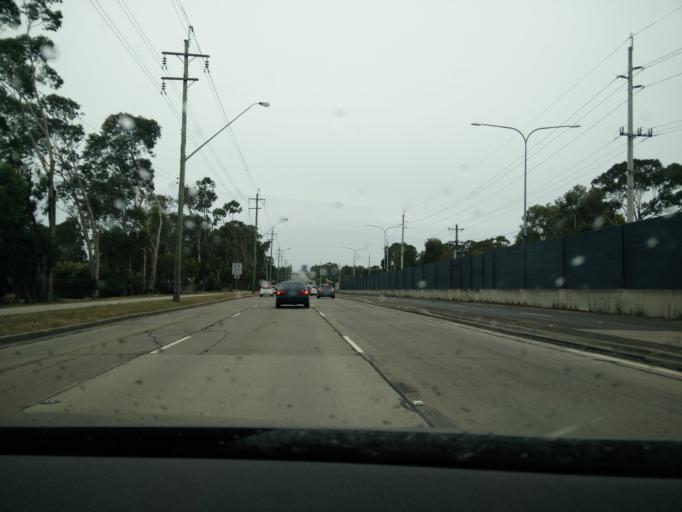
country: AU
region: New South Wales
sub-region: Parramatta
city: Constitution Hill
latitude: -33.7838
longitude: 150.9696
